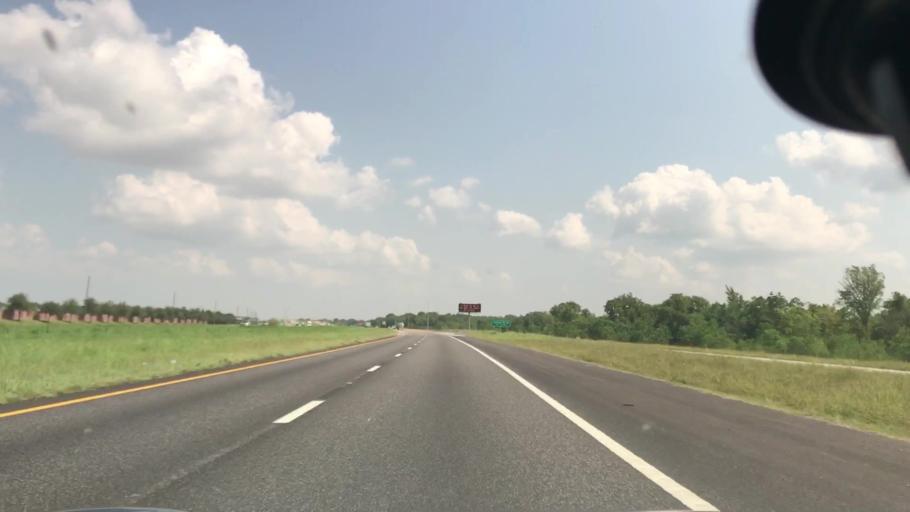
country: US
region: Texas
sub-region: Brazoria County
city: Iowa Colony
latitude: 29.4986
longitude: -95.3885
